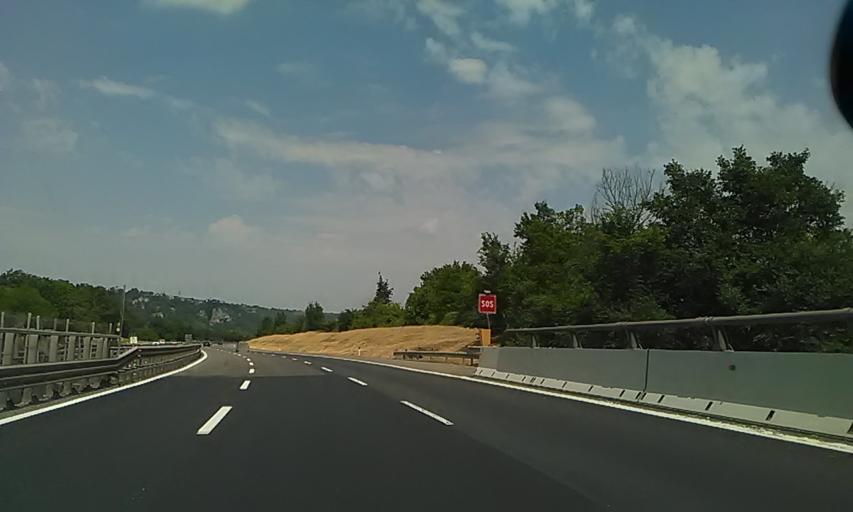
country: IT
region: Piedmont
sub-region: Provincia di Alessandria
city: Tagliolo Monferrato
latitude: 44.6504
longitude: 8.6616
